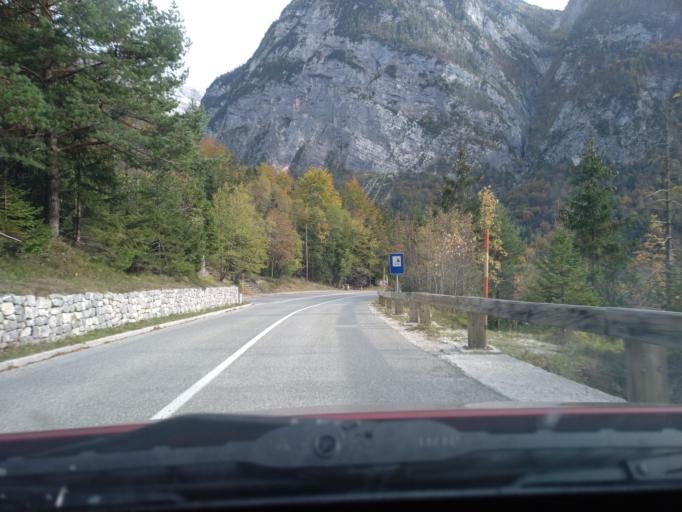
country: SI
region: Kranjska Gora
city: Kranjska Gora
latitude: 46.3855
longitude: 13.7518
